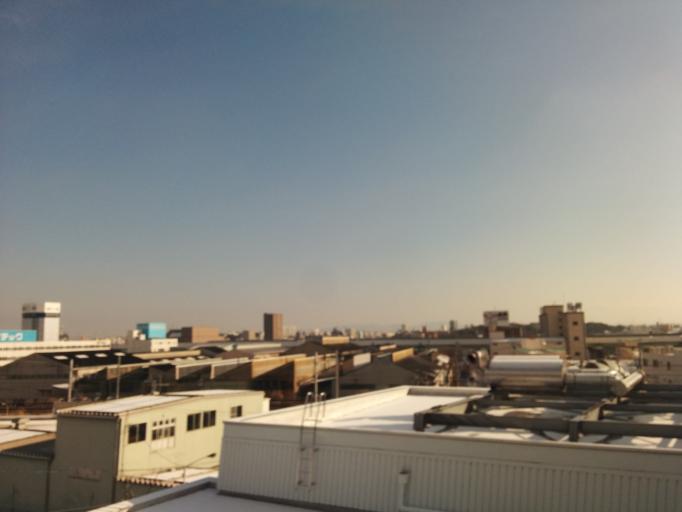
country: JP
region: Aichi
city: Nagoya-shi
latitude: 35.1027
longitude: 136.9211
